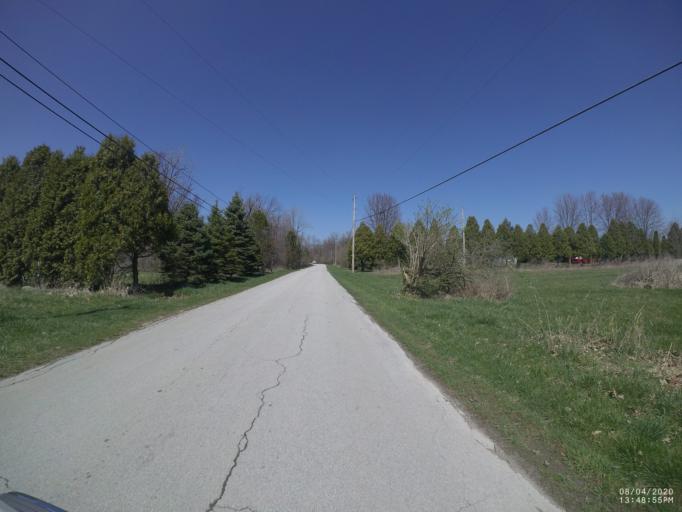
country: US
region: Ohio
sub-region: Sandusky County
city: Gibsonburg
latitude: 41.3167
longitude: -83.2850
